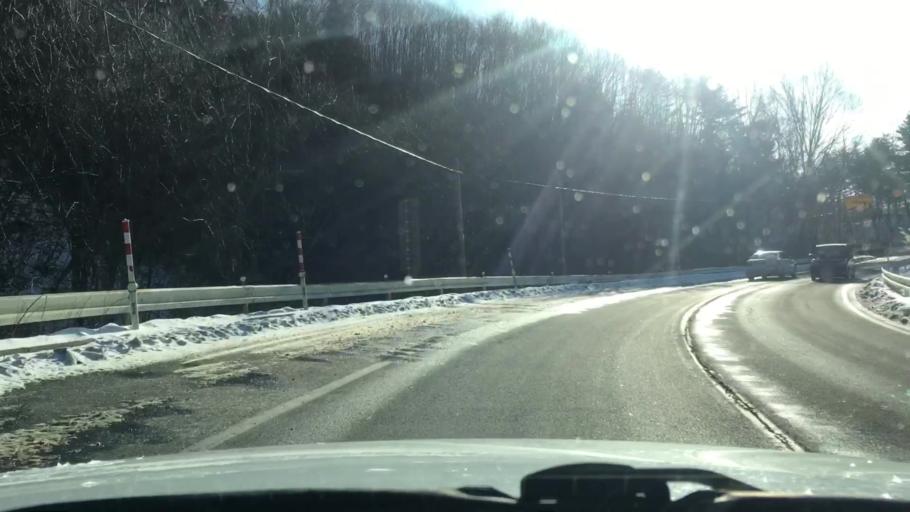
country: JP
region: Iwate
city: Morioka-shi
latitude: 39.6628
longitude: 141.3317
